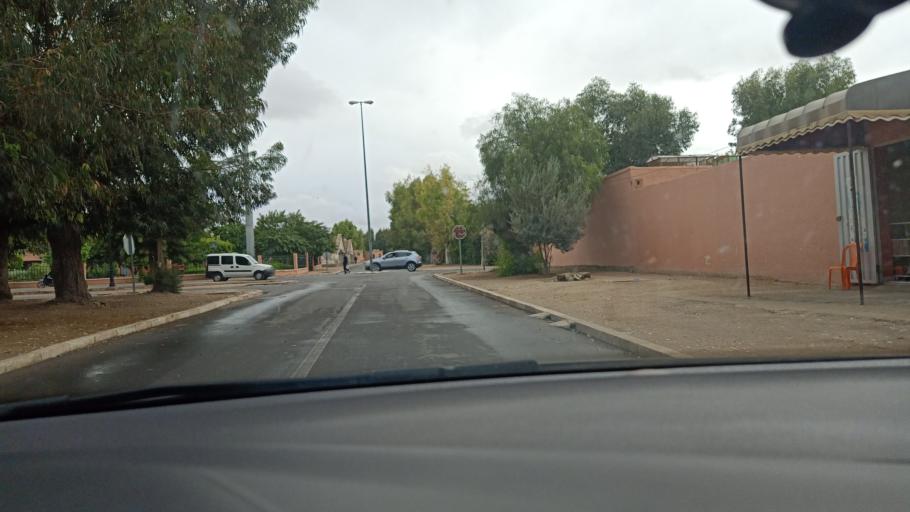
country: MA
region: Doukkala-Abda
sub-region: Safi
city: Youssoufia
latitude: 32.2481
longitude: -8.5312
